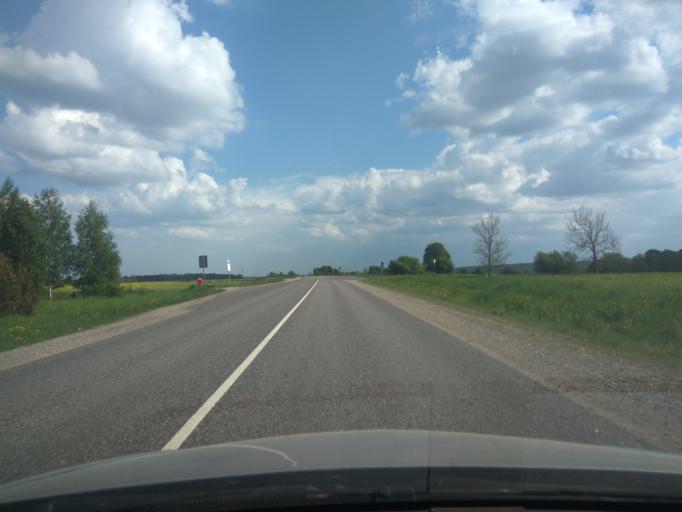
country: LV
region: Kuldigas Rajons
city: Kuldiga
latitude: 56.9973
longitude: 21.9016
